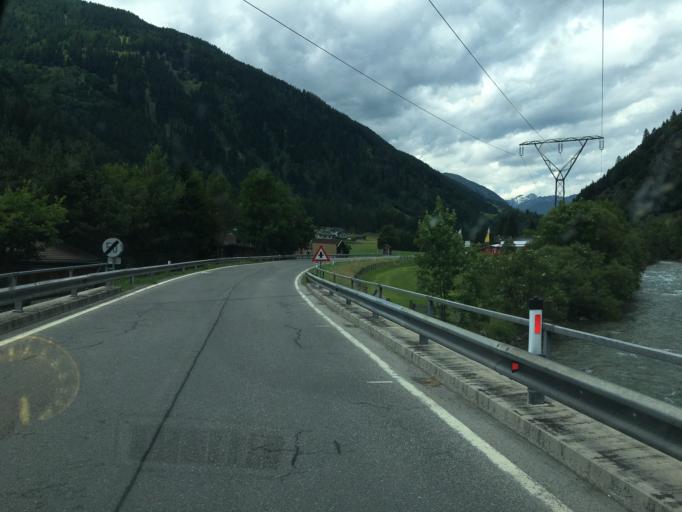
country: AT
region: Carinthia
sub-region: Politischer Bezirk Spittal an der Drau
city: Mortschach
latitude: 46.9343
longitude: 12.9043
